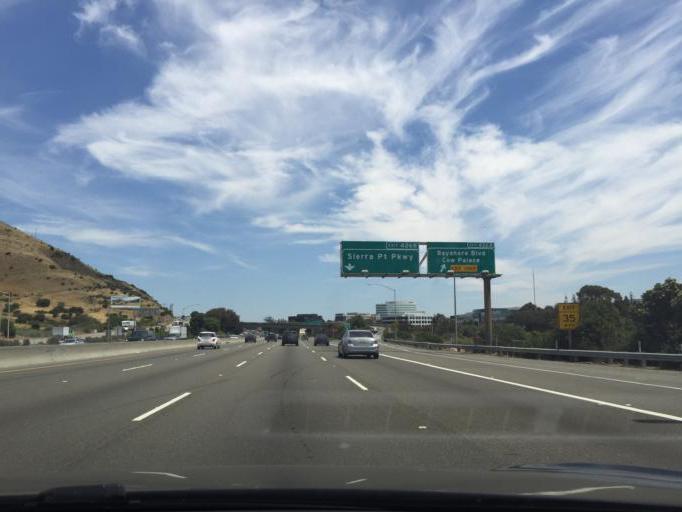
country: US
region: California
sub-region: San Mateo County
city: Brisbane
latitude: 37.6677
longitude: -122.3946
